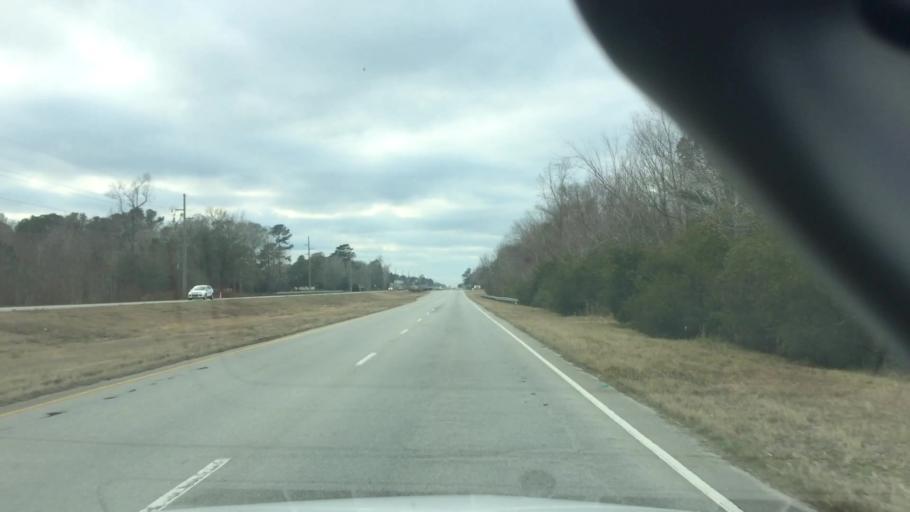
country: US
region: North Carolina
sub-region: Brunswick County
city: Sunset Beach
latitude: 33.9484
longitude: -78.4900
